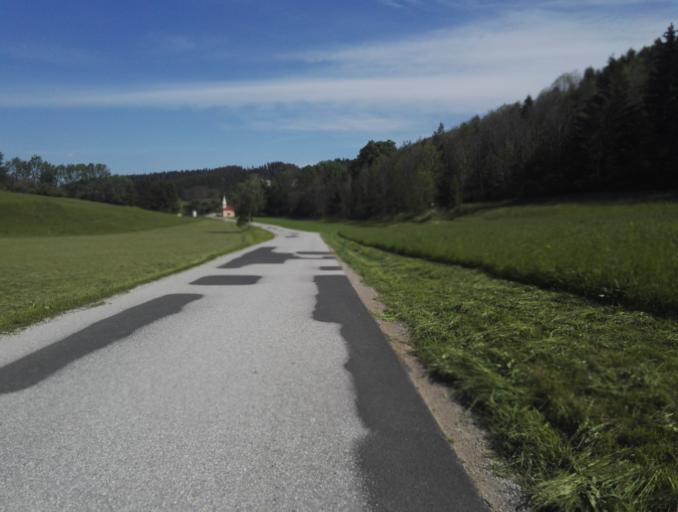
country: AT
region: Styria
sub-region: Politischer Bezirk Graz-Umgebung
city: Stattegg
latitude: 47.1579
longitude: 15.4339
